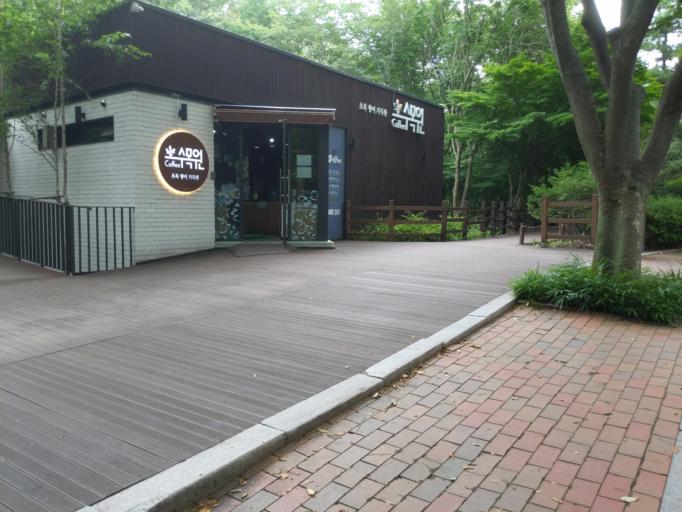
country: KR
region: Daegu
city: Hwawon
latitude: 35.8006
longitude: 128.5223
